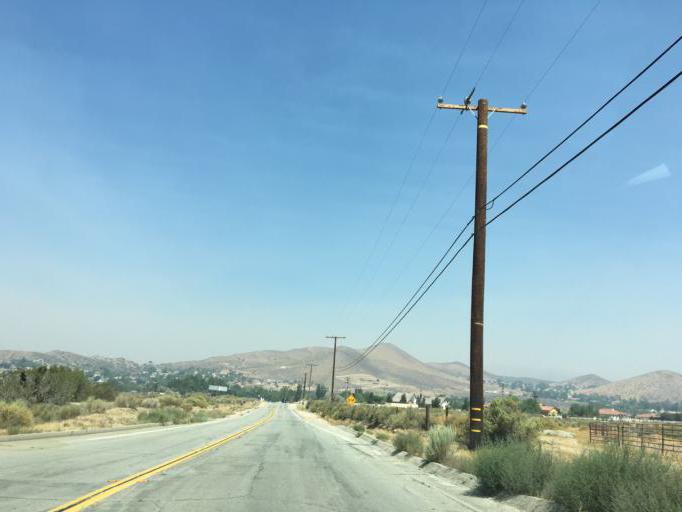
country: US
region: California
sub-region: Los Angeles County
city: Acton
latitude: 34.4715
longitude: -118.1615
